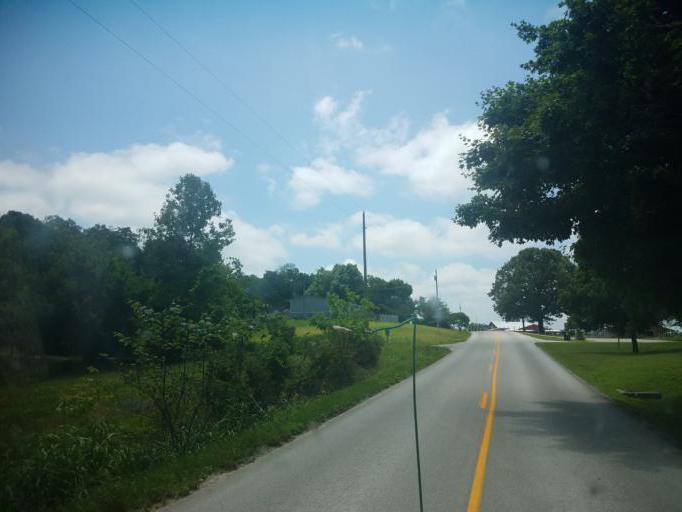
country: US
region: Kentucky
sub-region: Hart County
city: Munfordville
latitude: 37.3212
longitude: -86.0615
